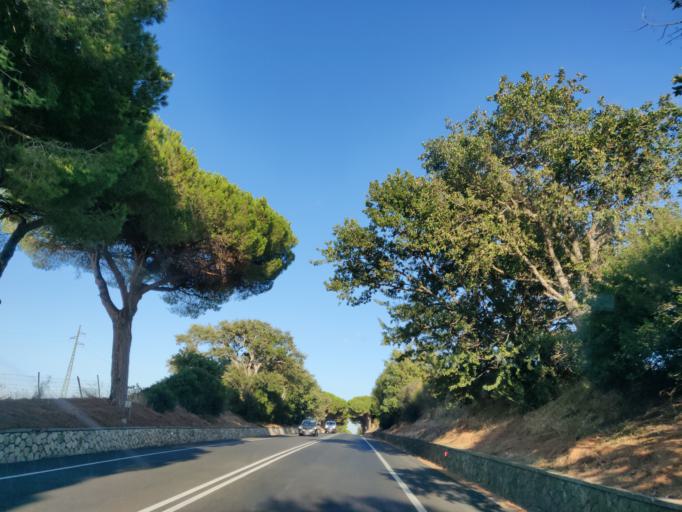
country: IT
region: Latium
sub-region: Provincia di Viterbo
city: Pescia Romana
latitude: 42.4142
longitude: 11.4528
